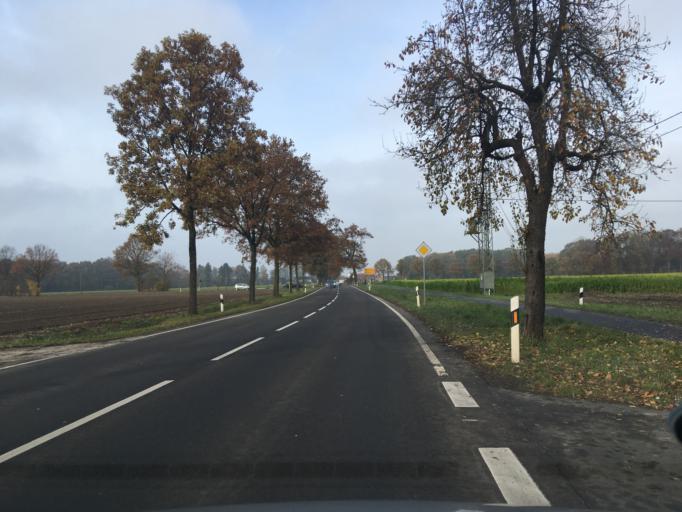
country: DE
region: North Rhine-Westphalia
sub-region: Regierungsbezirk Munster
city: Sudlohn
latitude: 51.9291
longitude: 6.8830
